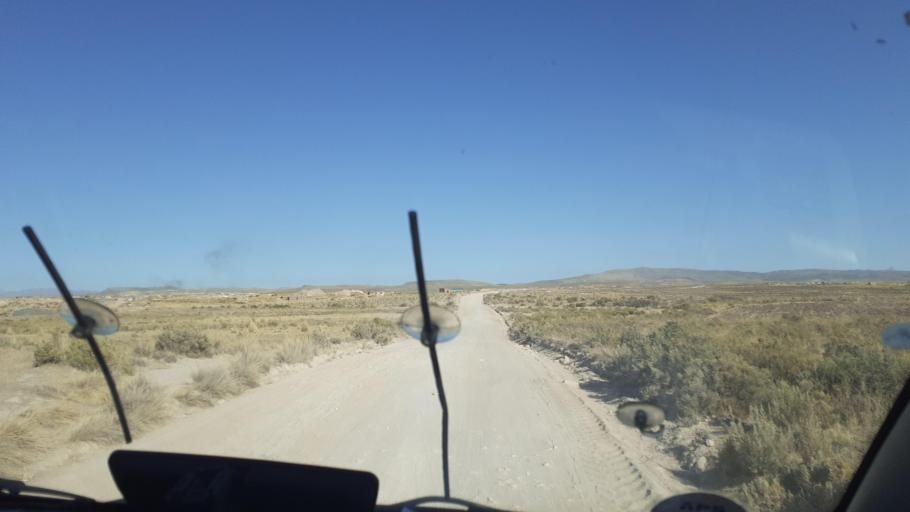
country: BO
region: La Paz
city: Tiahuanaco
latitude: -17.1156
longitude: -68.7961
